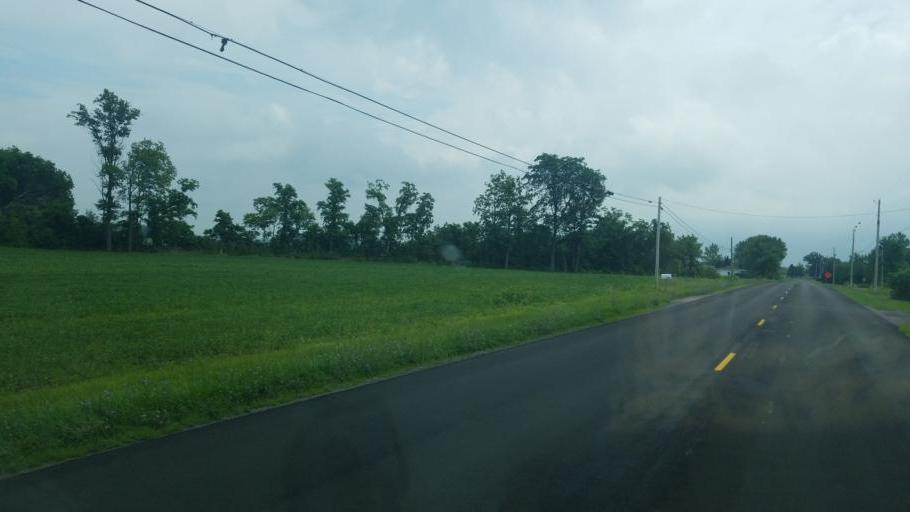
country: US
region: Ohio
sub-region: Logan County
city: Russells Point
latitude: 40.4671
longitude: -83.8356
